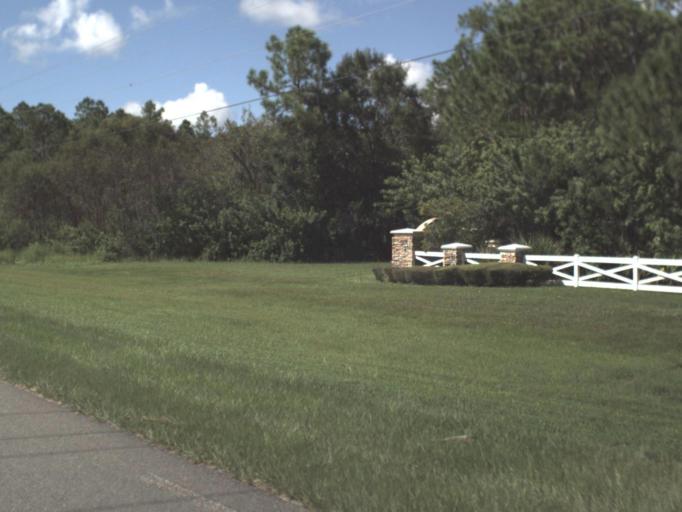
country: US
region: Florida
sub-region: Sarasota County
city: The Meadows
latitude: 27.4148
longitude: -82.3502
